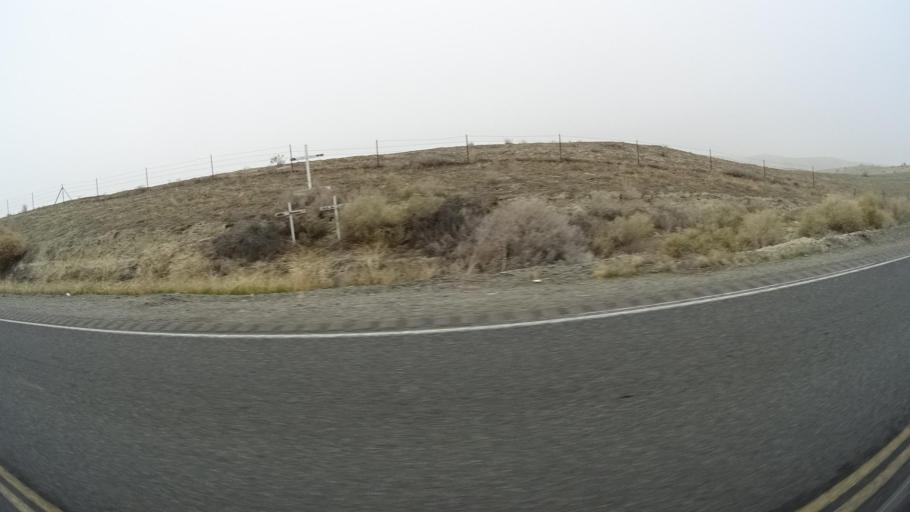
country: US
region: California
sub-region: Kern County
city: Buttonwillow
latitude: 35.3095
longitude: -119.4686
